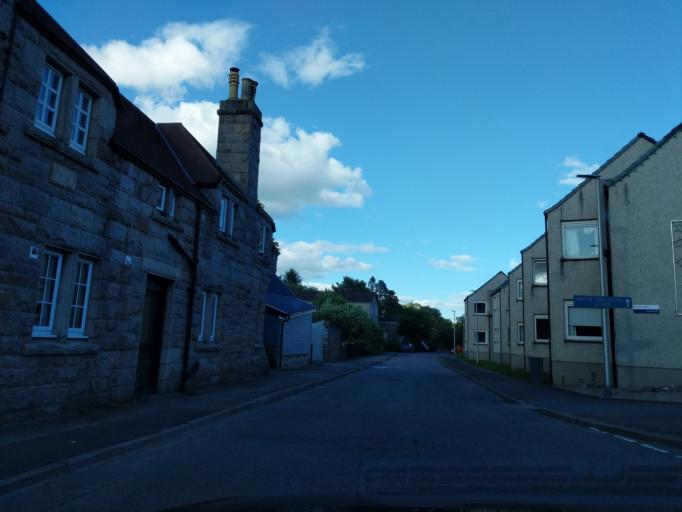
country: GB
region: Scotland
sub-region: Aberdeenshire
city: Aboyne
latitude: 57.0766
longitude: -2.7773
